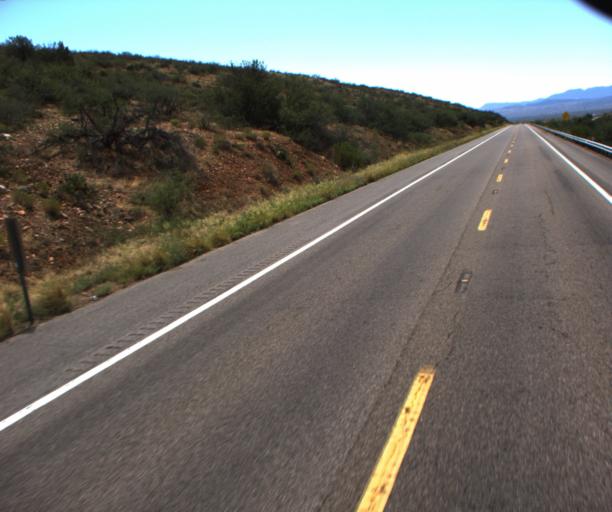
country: US
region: Arizona
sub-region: Gila County
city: Globe
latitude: 33.4582
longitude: -110.7212
